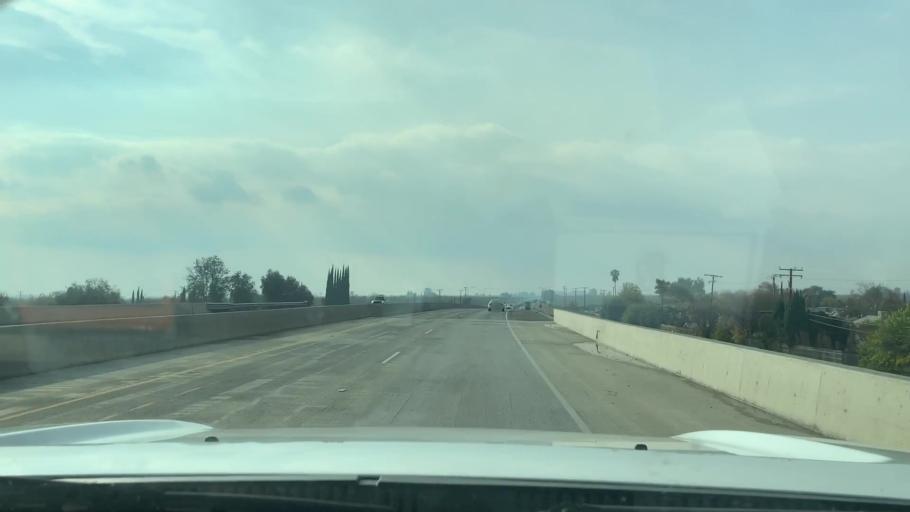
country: US
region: California
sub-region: Kings County
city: Armona
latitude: 36.3091
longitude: -119.7090
